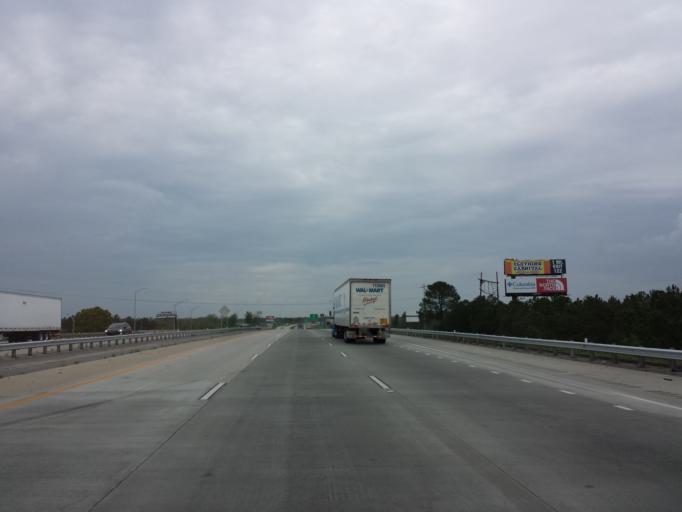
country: US
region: Georgia
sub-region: Dooly County
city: Unadilla
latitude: 32.2462
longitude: -83.7424
